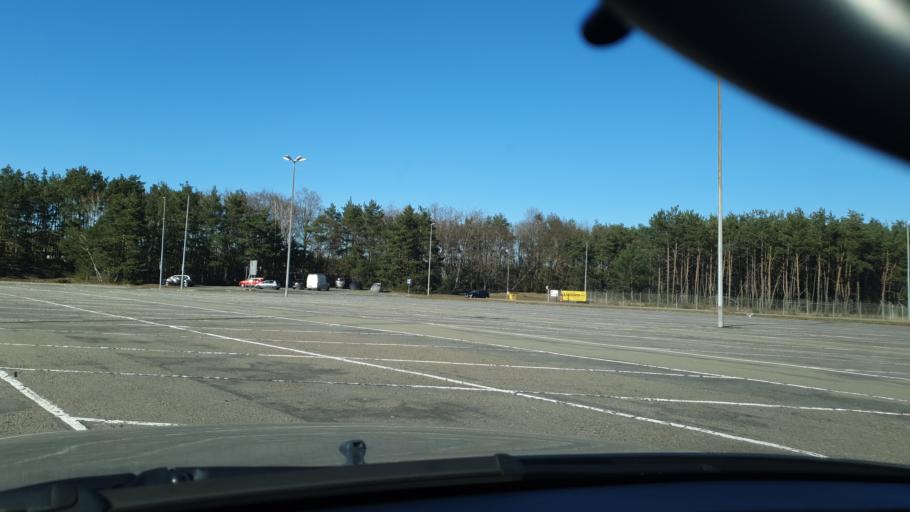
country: DE
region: Rheinland-Pfalz
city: Rodenbach
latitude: 49.4403
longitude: 7.6934
